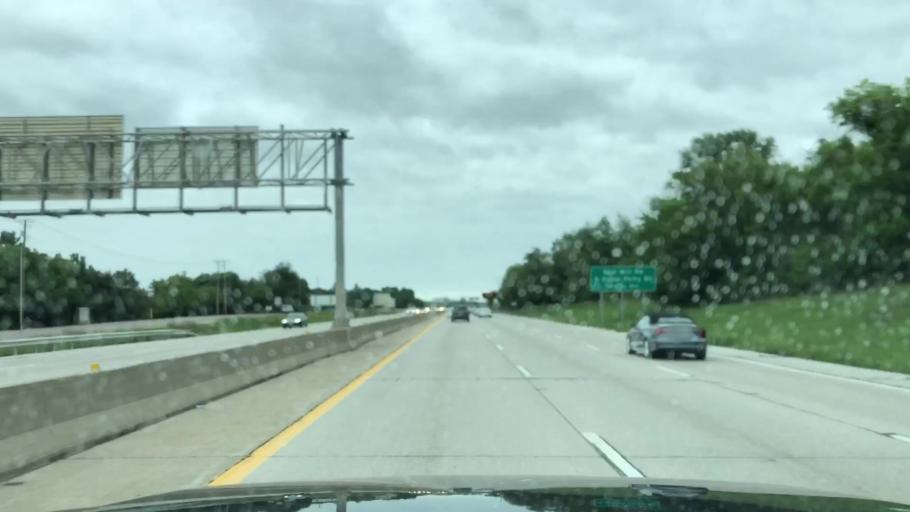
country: US
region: Missouri
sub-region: Saint Louis County
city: Manchester
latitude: 38.6299
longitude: -90.5144
